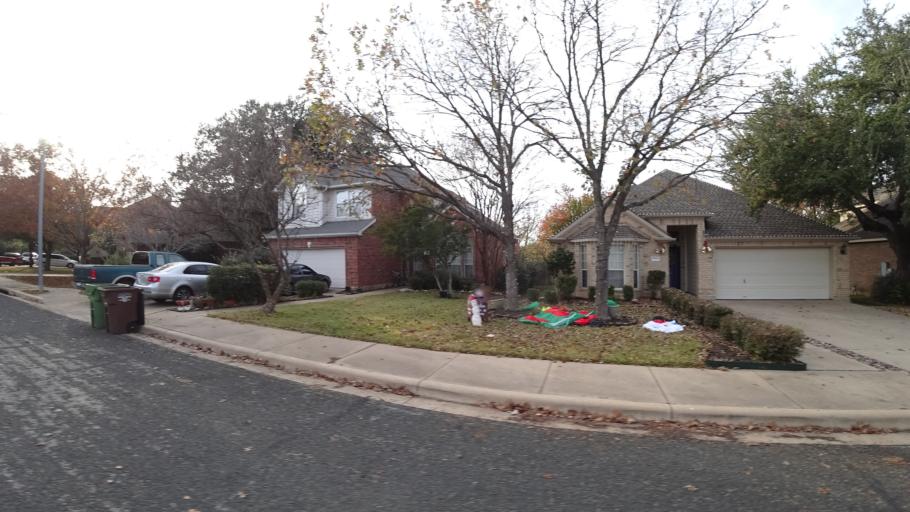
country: US
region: Texas
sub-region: Williamson County
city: Brushy Creek
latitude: 30.5176
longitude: -97.7259
